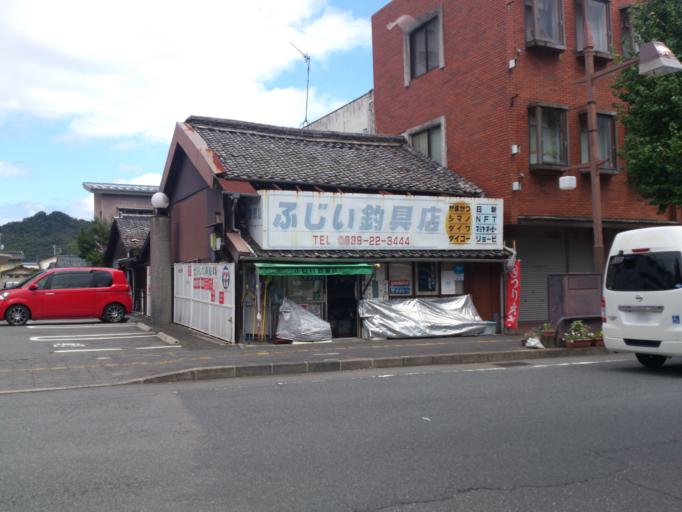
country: JP
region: Yamaguchi
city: Yamaguchi-shi
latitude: 34.1751
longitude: 131.4781
